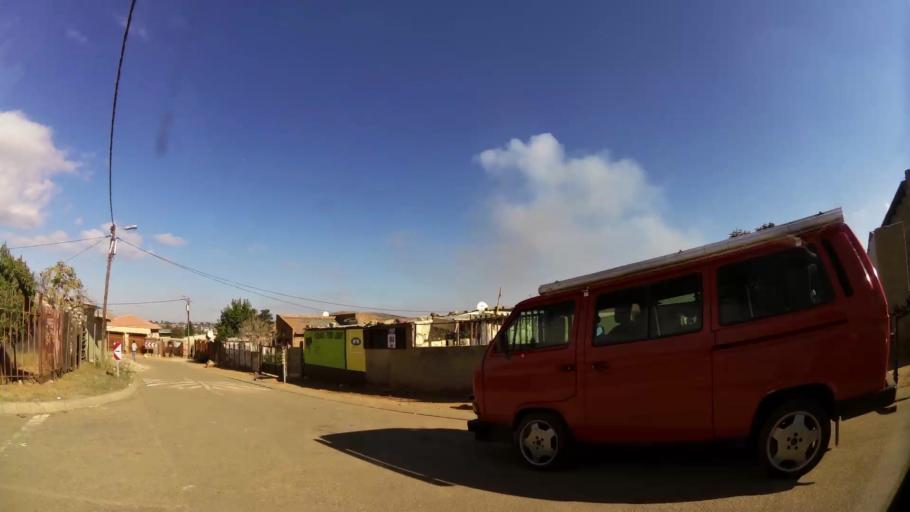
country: ZA
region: Gauteng
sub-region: City of Tshwane Metropolitan Municipality
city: Cullinan
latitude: -25.6953
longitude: 28.4093
